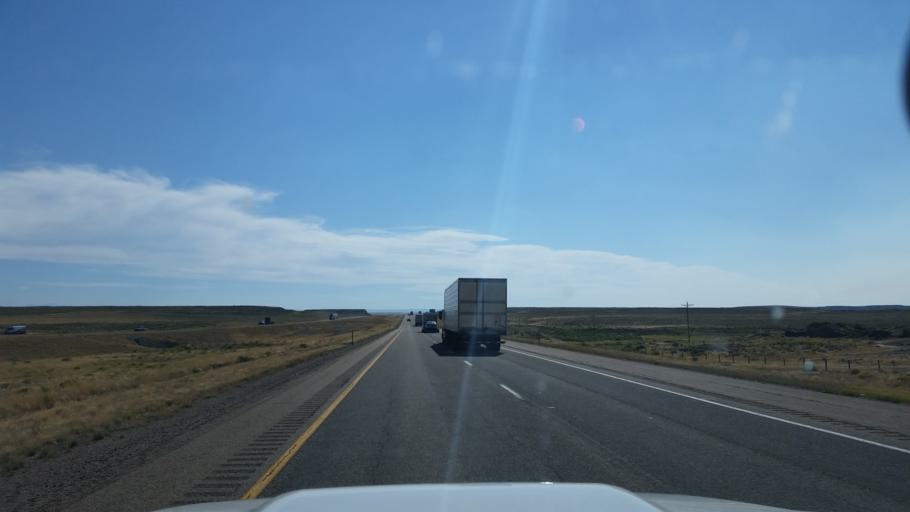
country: US
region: Wyoming
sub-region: Uinta County
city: Lyman
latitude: 41.4092
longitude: -110.1521
